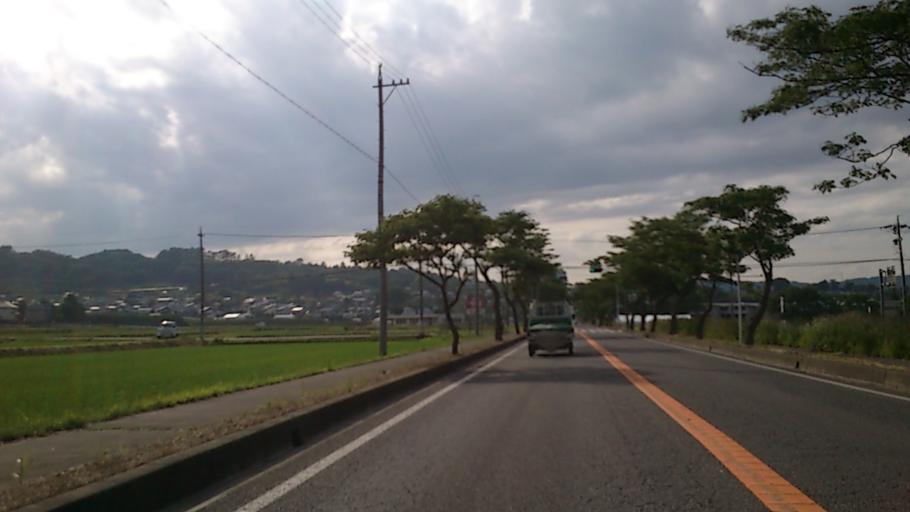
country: JP
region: Nagano
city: Saku
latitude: 36.2435
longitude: 138.4227
